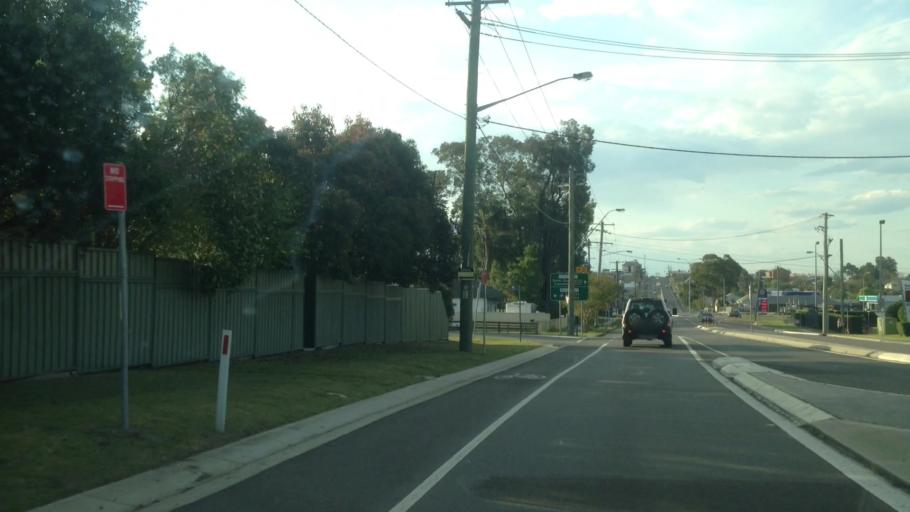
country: AU
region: New South Wales
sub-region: Cessnock
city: Kurri Kurri
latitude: -32.8261
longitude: 151.4872
